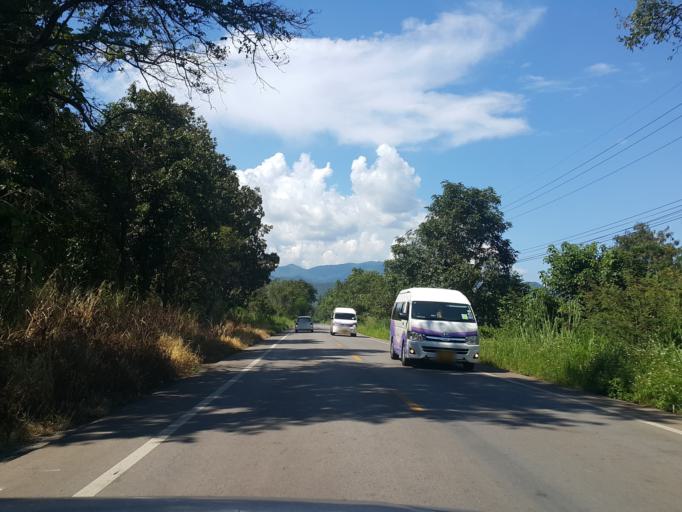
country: TH
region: Chiang Mai
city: Mae Taeng
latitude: 19.1557
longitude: 98.9426
